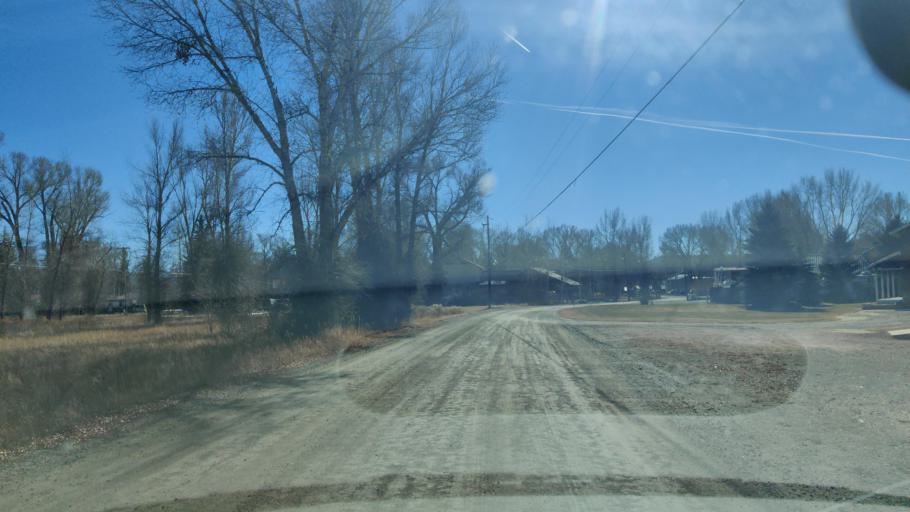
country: US
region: Colorado
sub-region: Gunnison County
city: Gunnison
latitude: 38.5368
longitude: -106.9505
